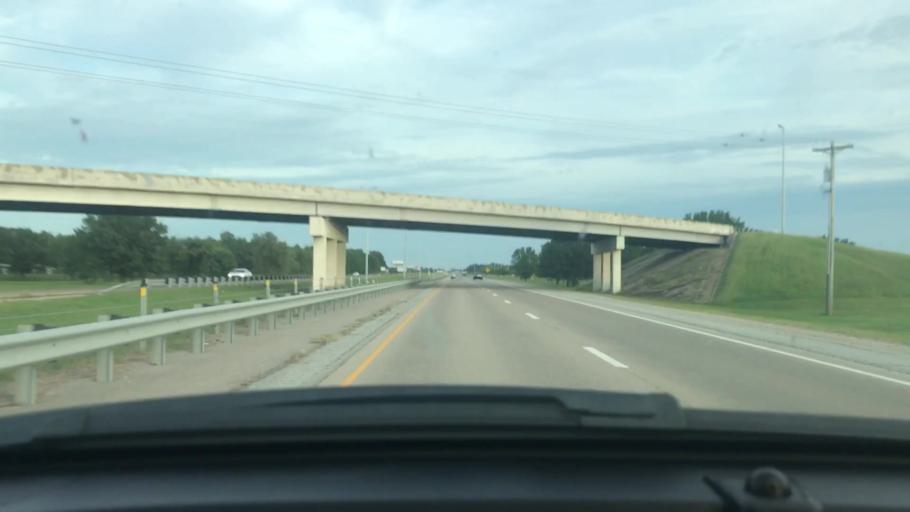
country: US
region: Arkansas
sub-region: Craighead County
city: Bay
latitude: 35.8019
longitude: -90.6253
